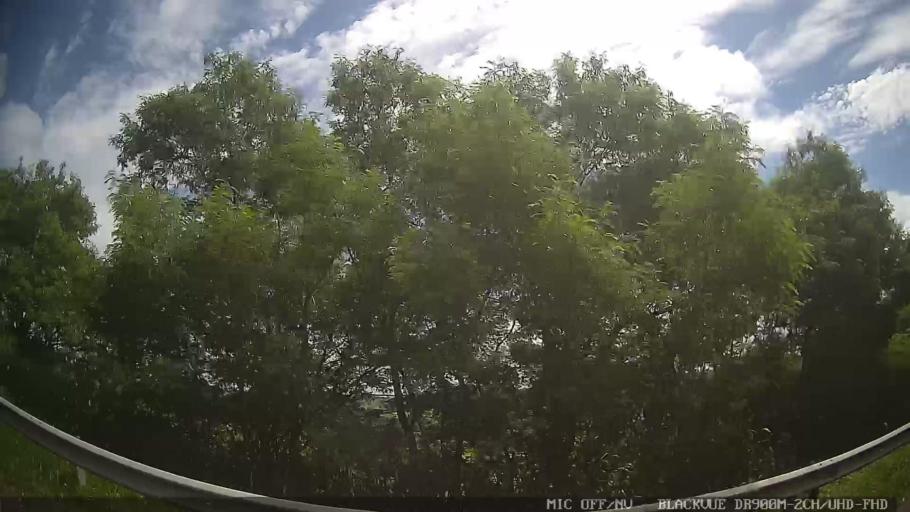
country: BR
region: Sao Paulo
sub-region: Laranjal Paulista
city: Laranjal Paulista
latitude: -23.0856
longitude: -47.7837
